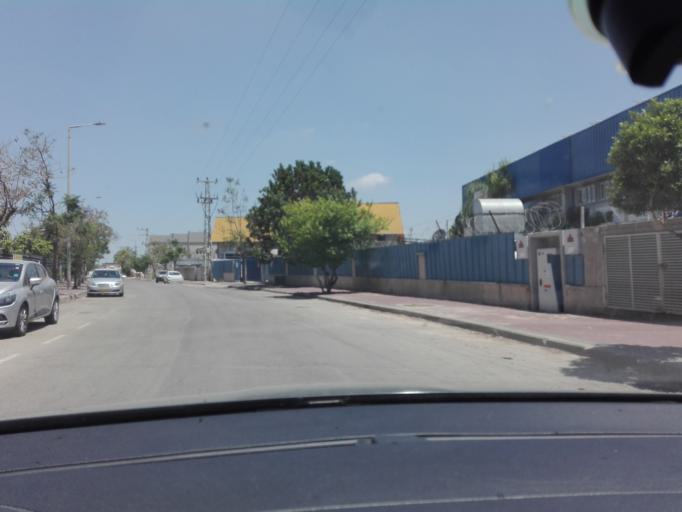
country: IL
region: Southern District
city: Qiryat Gat
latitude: 31.5925
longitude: 34.7809
